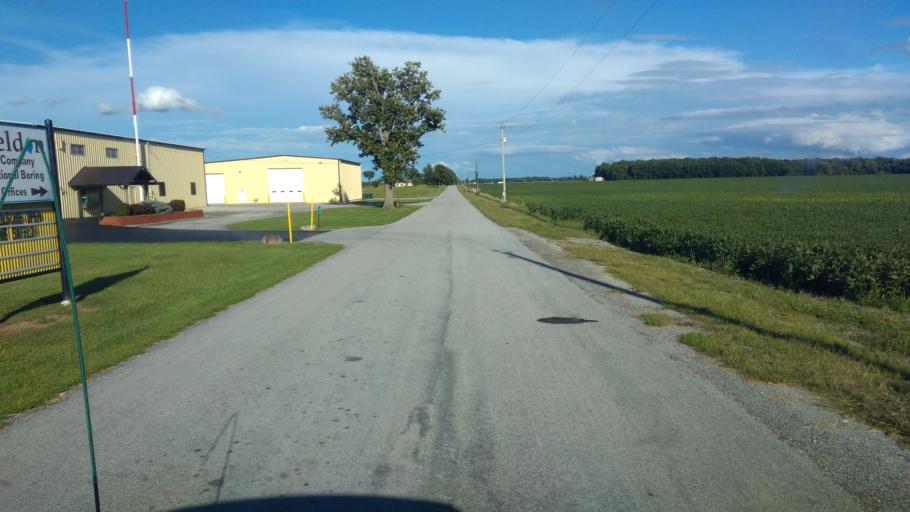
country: US
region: Ohio
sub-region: Hardin County
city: Kenton
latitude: 40.7610
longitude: -83.6355
